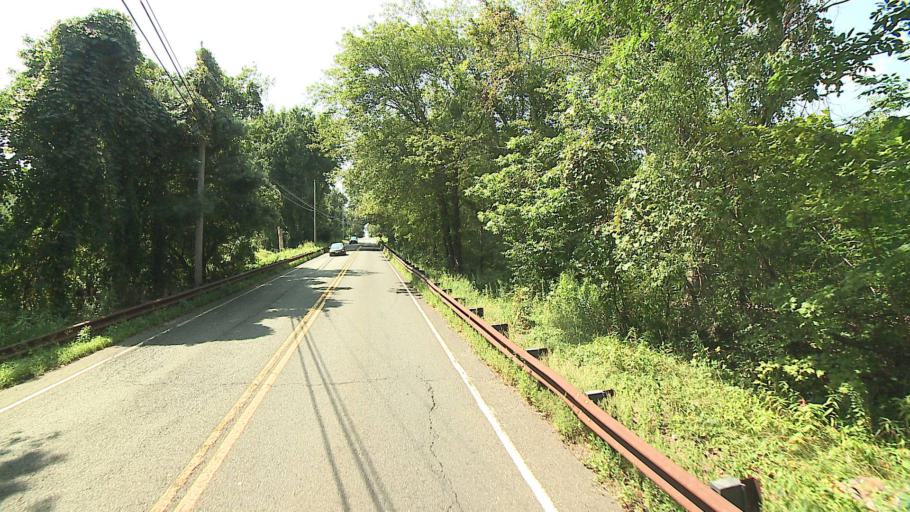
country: US
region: Connecticut
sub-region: Fairfield County
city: Trumbull
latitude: 41.3314
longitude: -73.1976
